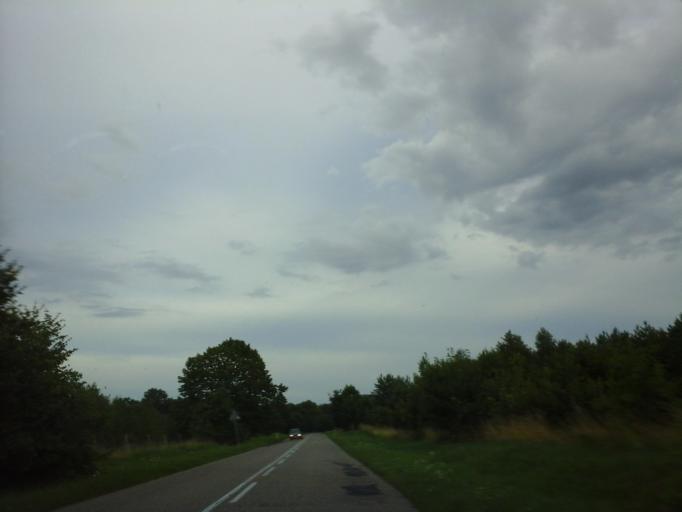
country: PL
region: West Pomeranian Voivodeship
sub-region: Powiat goleniowski
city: Nowogard
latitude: 53.7074
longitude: 15.0393
